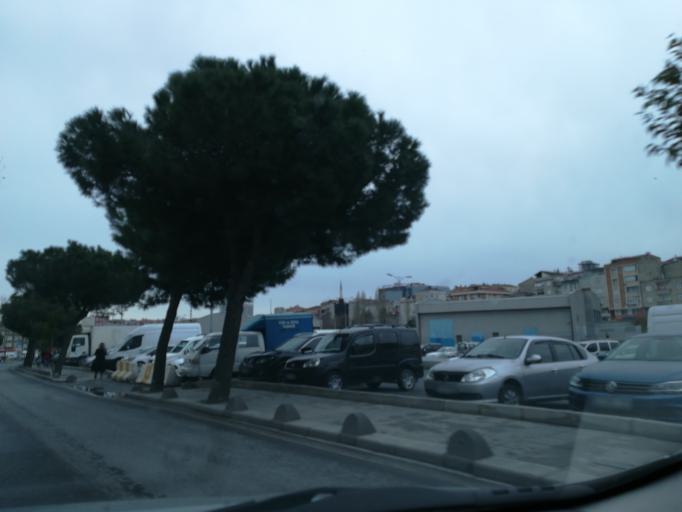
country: TR
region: Istanbul
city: Bagcilar
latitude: 41.0338
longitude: 28.8431
